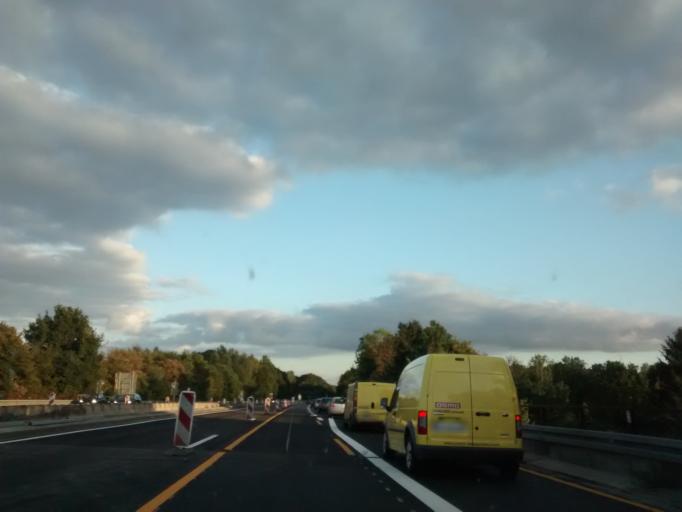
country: DE
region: Lower Saxony
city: Osnabrueck
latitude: 52.2637
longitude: 8.0035
